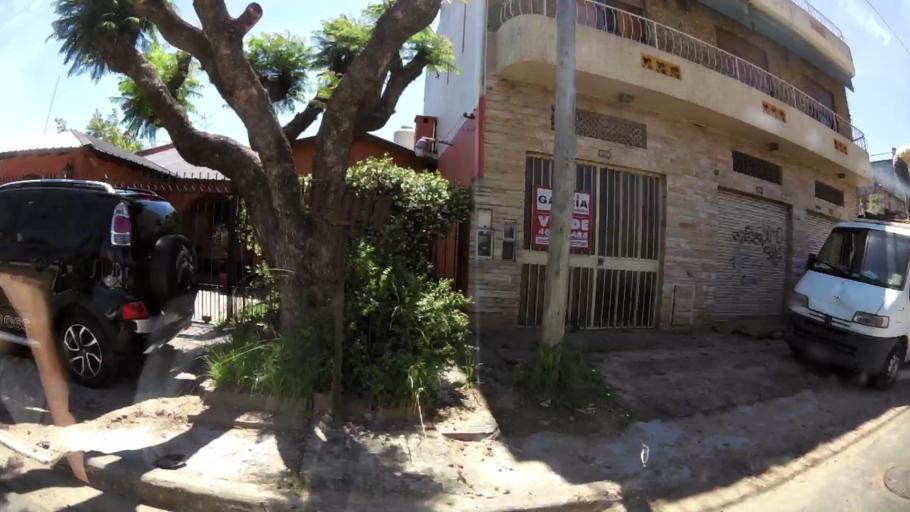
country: AR
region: Buenos Aires
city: Ituzaingo
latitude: -34.6664
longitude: -58.6889
